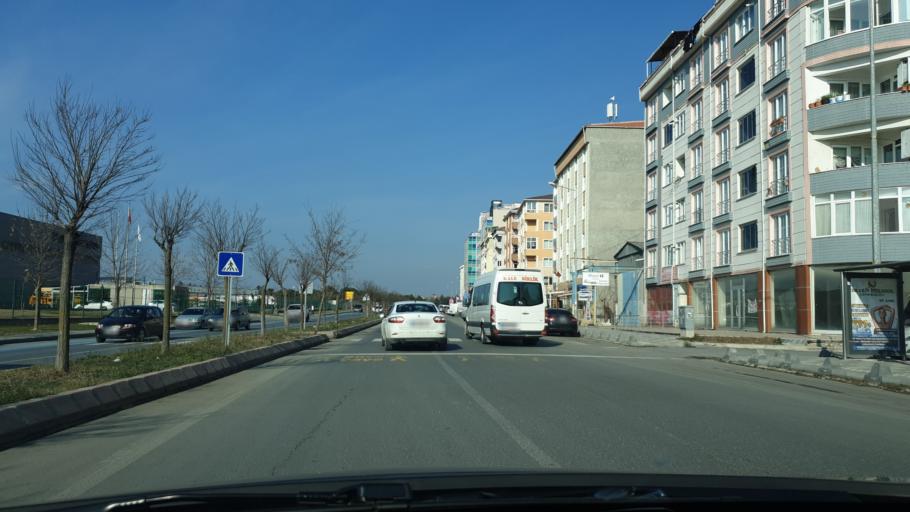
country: TR
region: Tekirdag
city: Cerkezkoey
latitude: 41.2917
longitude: 27.9936
